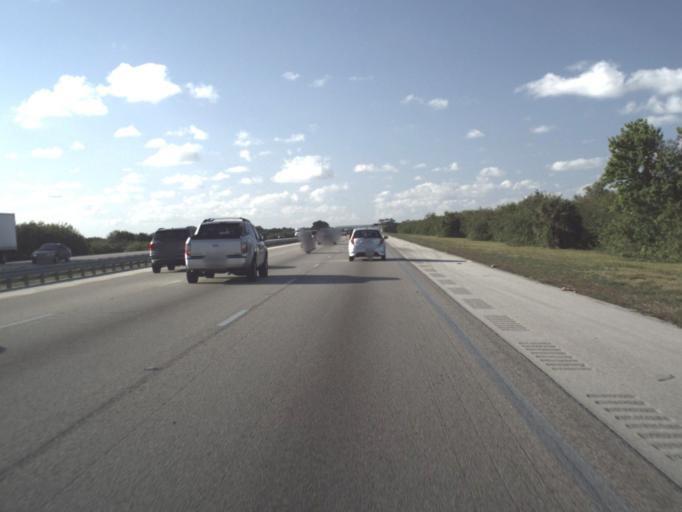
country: US
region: Florida
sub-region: Brevard County
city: Rockledge
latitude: 28.2540
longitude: -80.7252
